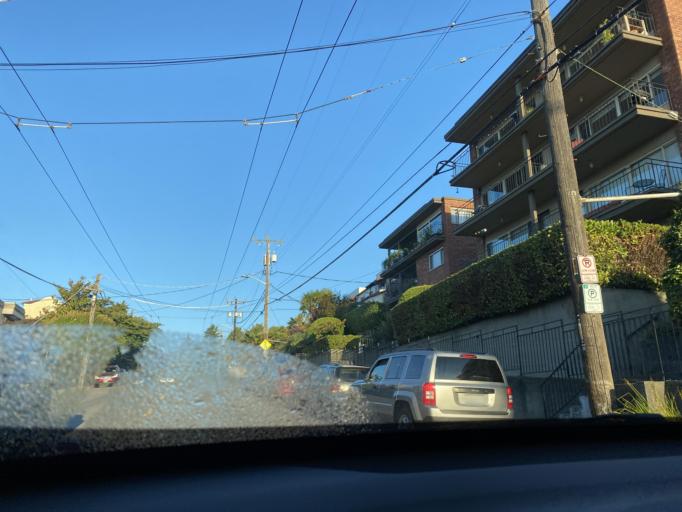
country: US
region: Washington
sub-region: King County
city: Seattle
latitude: 47.6267
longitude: -122.3617
